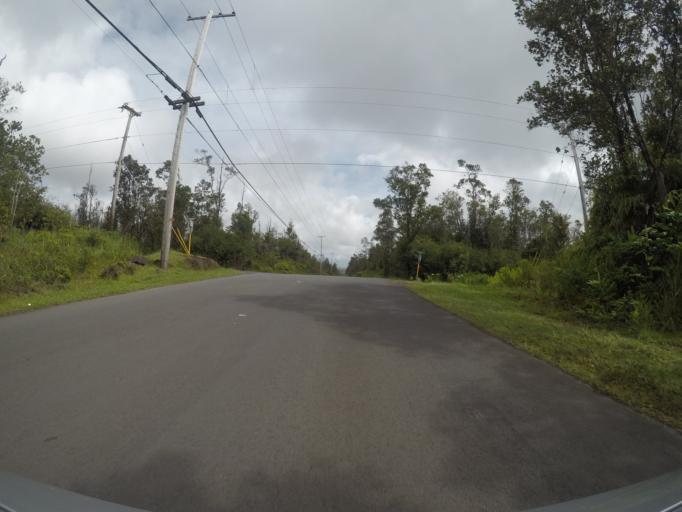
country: US
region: Hawaii
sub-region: Hawaii County
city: Fern Acres
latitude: 19.4678
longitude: -155.1356
